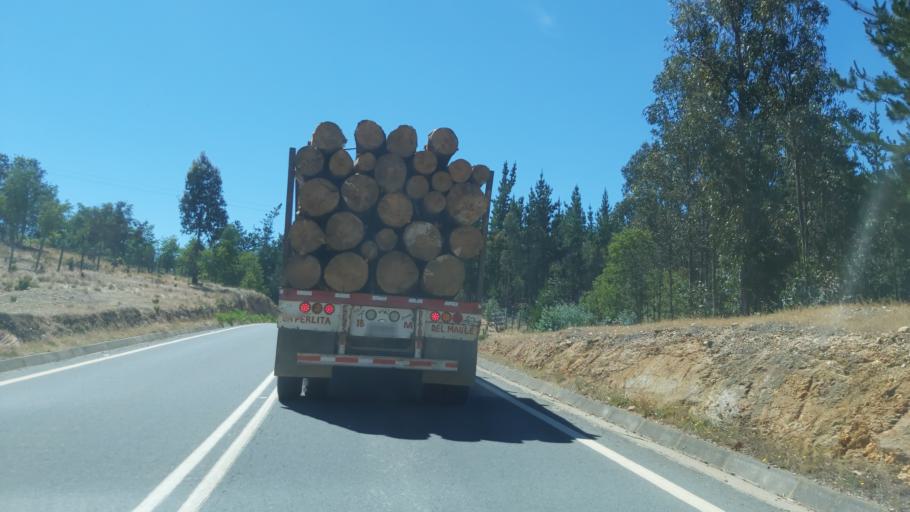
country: CL
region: Maule
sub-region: Provincia de Talca
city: Constitucion
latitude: -34.9364
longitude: -71.9832
